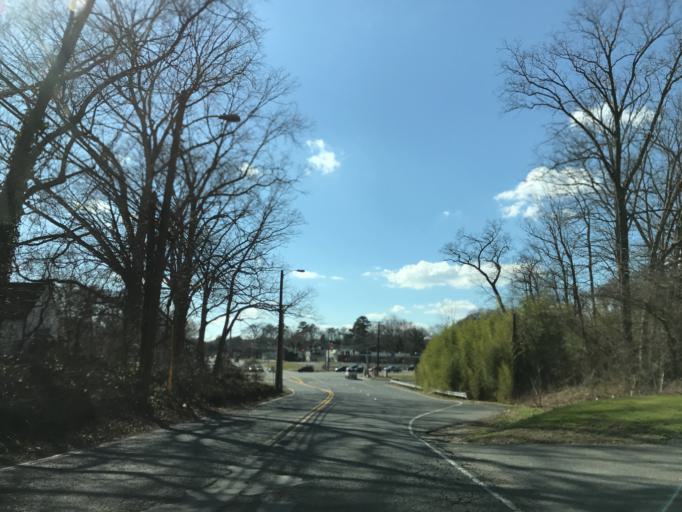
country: US
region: Maryland
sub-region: Anne Arundel County
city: Pasadena
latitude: 39.1097
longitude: -76.5728
